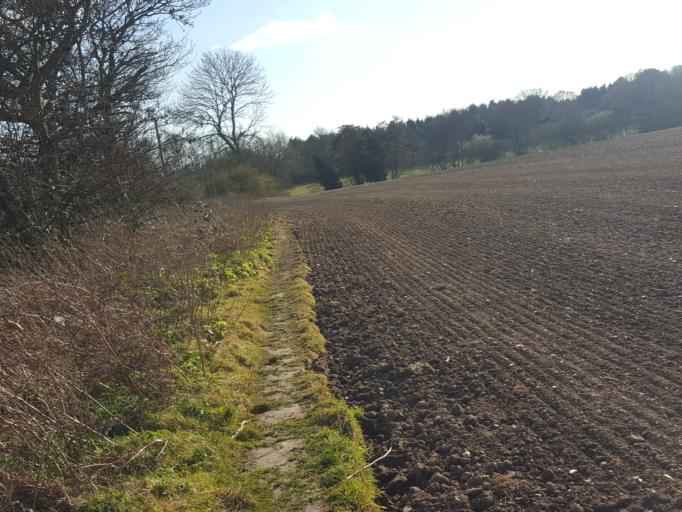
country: GB
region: England
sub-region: Essex
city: Little Clacton
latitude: 51.8647
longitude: 1.1141
